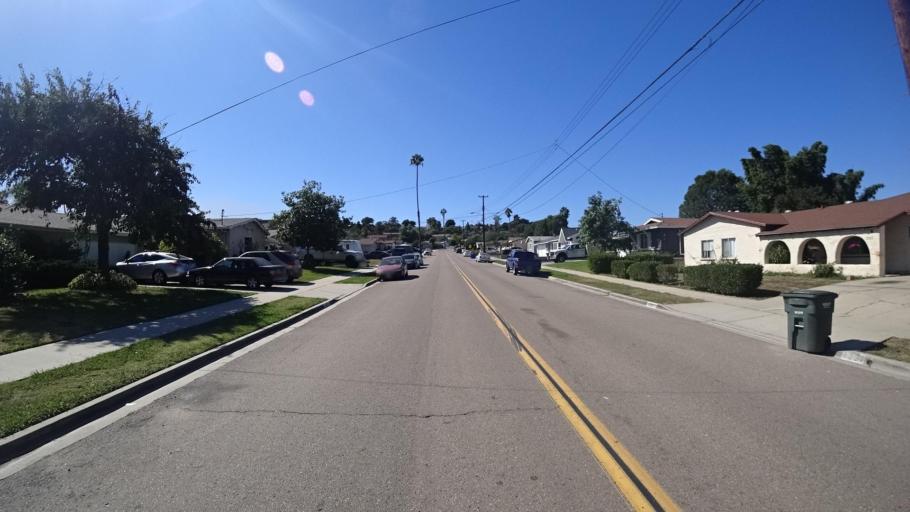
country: US
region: California
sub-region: San Diego County
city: La Presa
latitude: 32.7199
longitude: -117.0162
